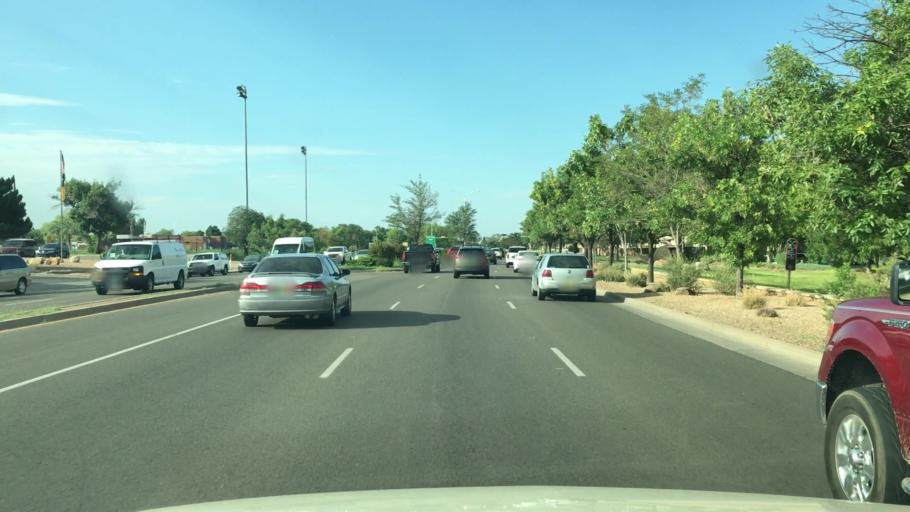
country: US
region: New Mexico
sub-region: Santa Fe County
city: Santa Fe
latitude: 35.6733
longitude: -105.9541
